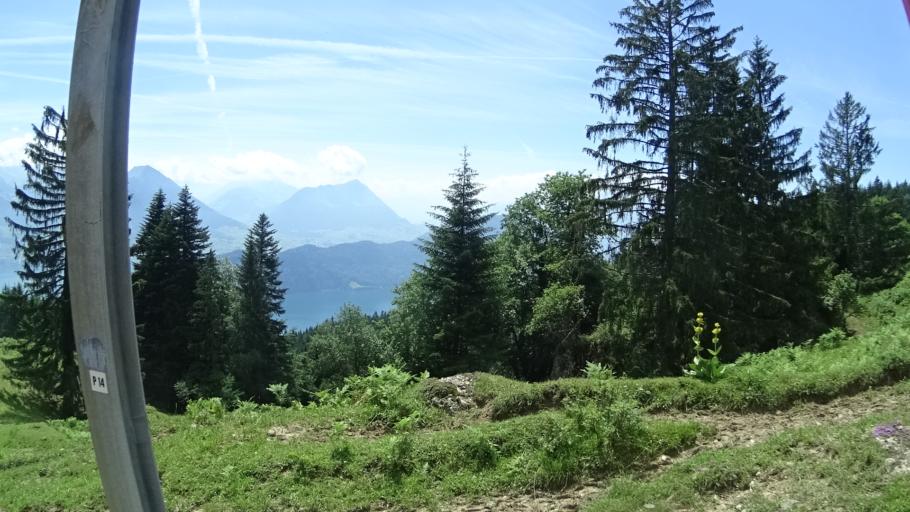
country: CH
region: Lucerne
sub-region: Lucerne-Land District
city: Vitznau
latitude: 47.0349
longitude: 8.4773
